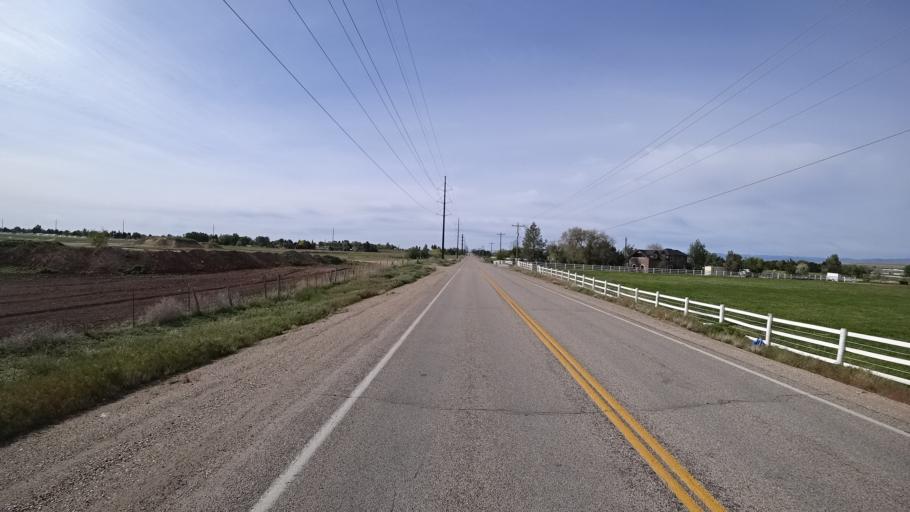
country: US
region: Idaho
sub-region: Ada County
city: Kuna
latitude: 43.4926
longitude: -116.3343
